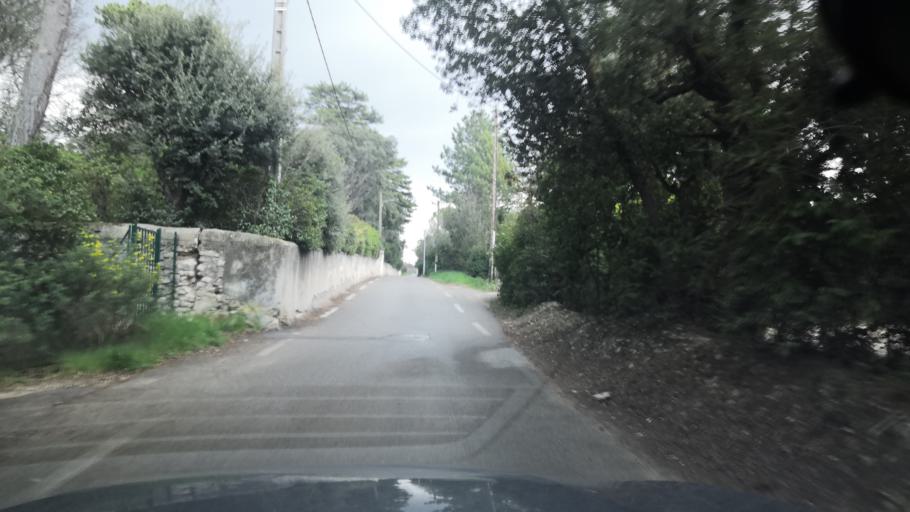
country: FR
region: Provence-Alpes-Cote d'Azur
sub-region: Departement des Bouches-du-Rhone
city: Aix-en-Provence
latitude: 43.5624
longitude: 5.4141
